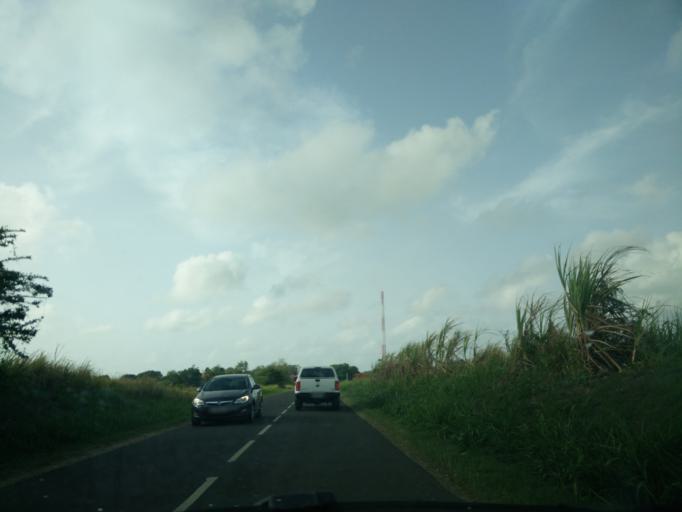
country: GP
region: Guadeloupe
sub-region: Guadeloupe
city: Le Moule
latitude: 16.3049
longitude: -61.3670
